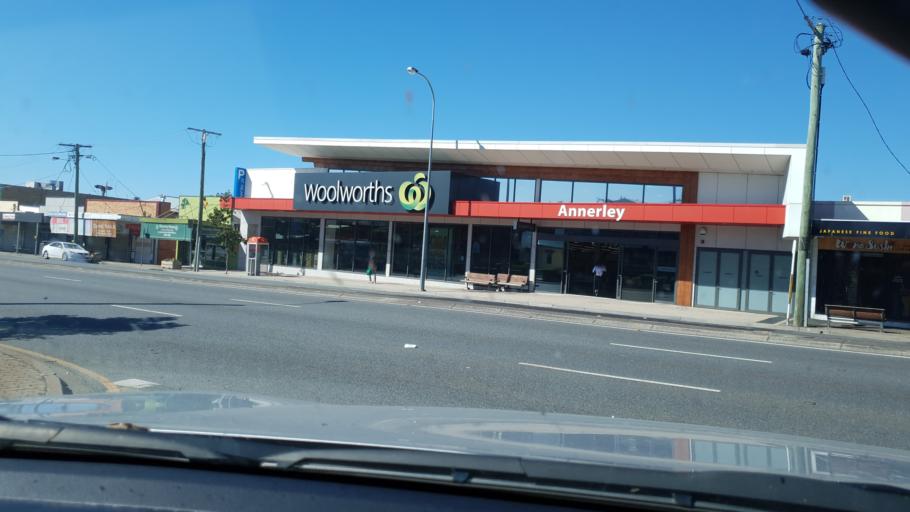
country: AU
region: Queensland
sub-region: Brisbane
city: Annerley
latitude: -27.5115
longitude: 153.0317
